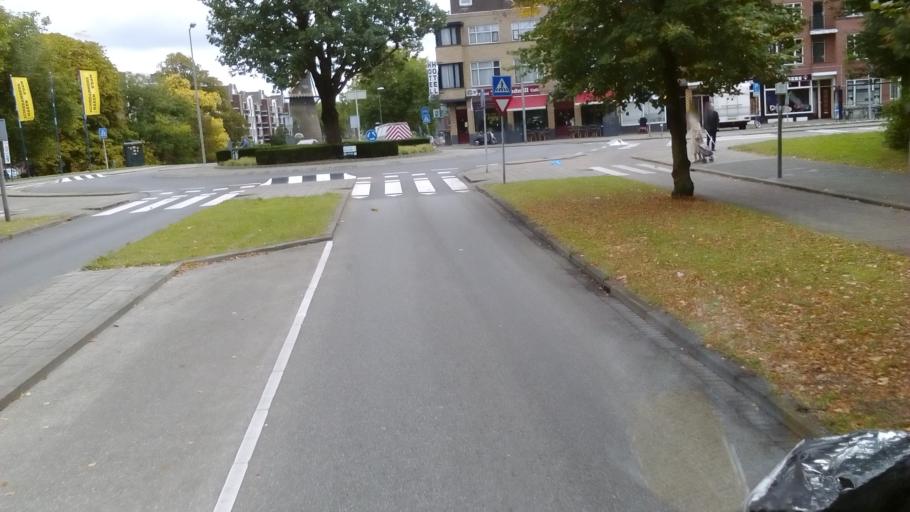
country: NL
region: South Holland
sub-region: Gemeente Schiedam
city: Schiedam
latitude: 51.9176
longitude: 4.3915
